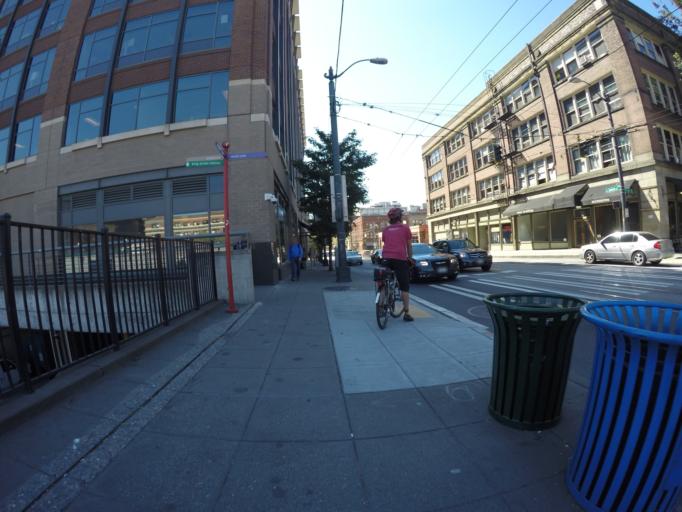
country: US
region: Washington
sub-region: King County
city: Seattle
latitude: 47.5992
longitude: -122.3302
